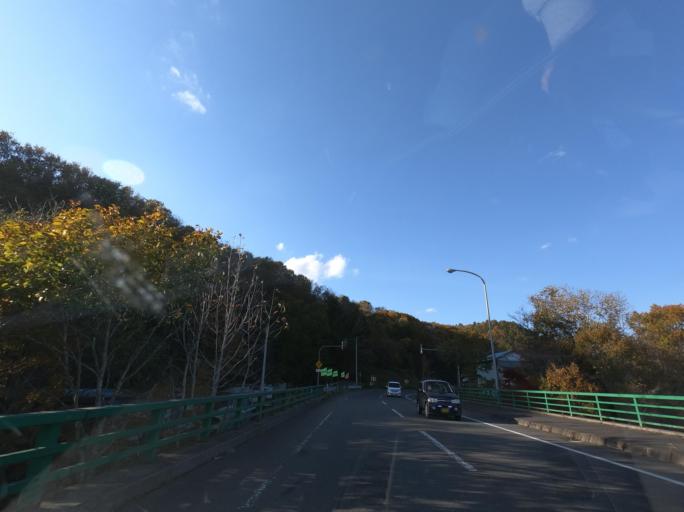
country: JP
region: Hokkaido
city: Iwamizawa
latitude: 42.9995
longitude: 142.0052
